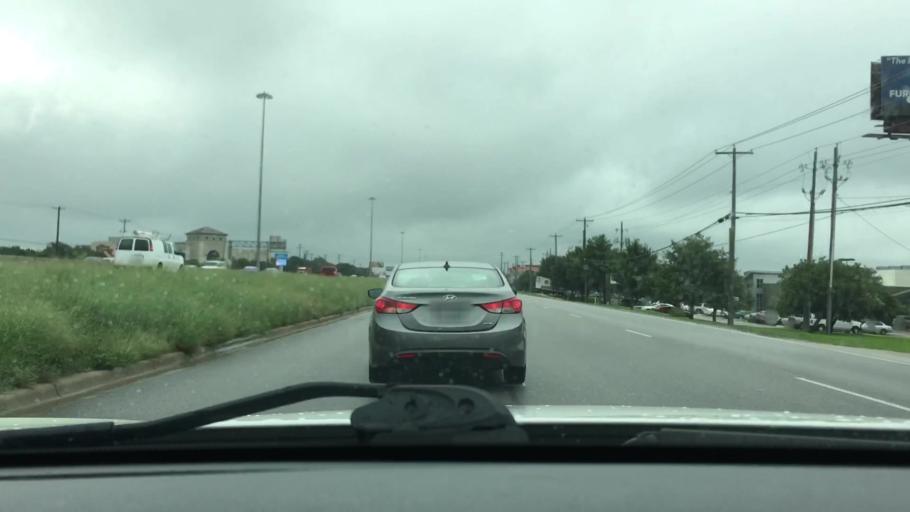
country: US
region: Texas
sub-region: Travis County
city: Wells Branch
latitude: 30.4334
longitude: -97.6701
